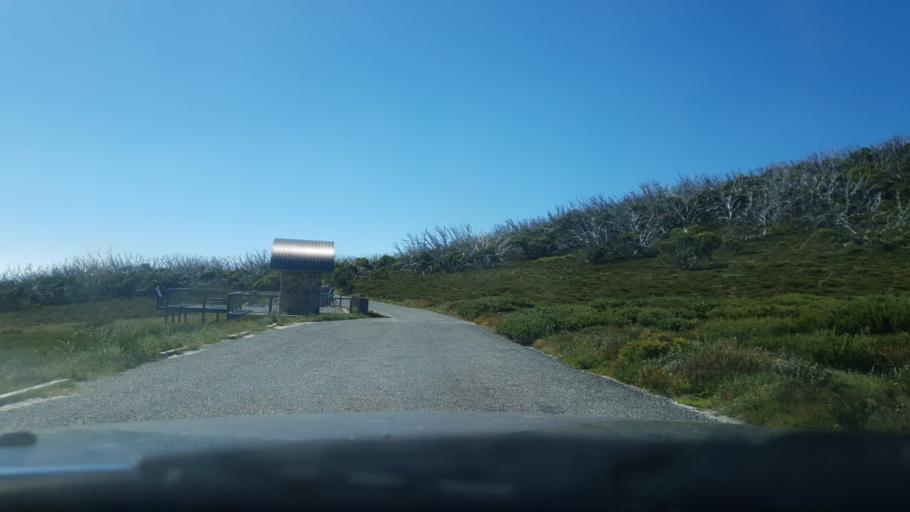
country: AU
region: Victoria
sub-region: Alpine
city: Mount Beauty
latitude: -36.8931
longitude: 147.3010
